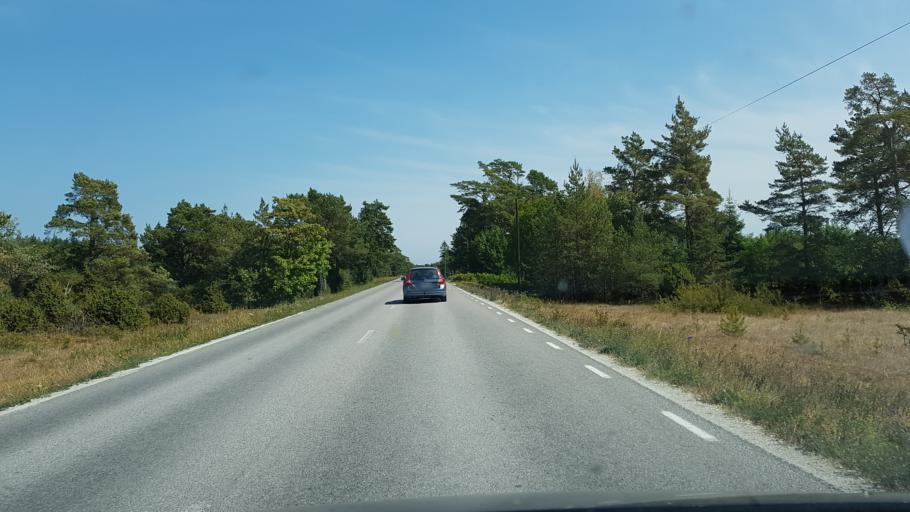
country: SE
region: Gotland
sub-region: Gotland
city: Visby
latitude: 57.6315
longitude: 18.4172
